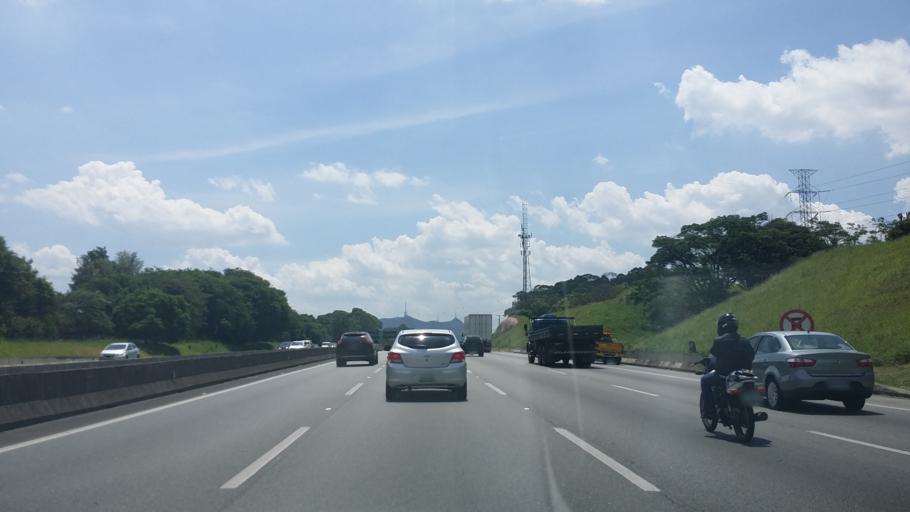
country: BR
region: Sao Paulo
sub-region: Osasco
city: Osasco
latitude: -23.5030
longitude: -46.7251
